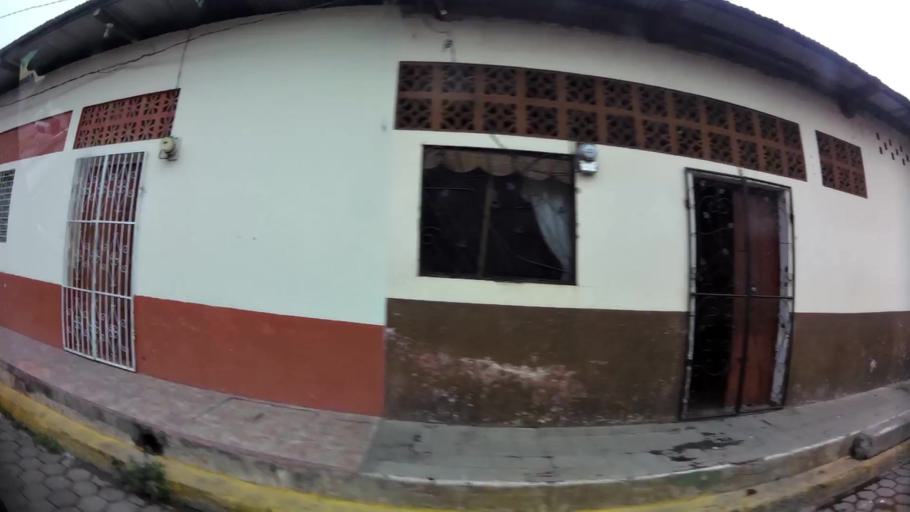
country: NI
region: Leon
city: Leon
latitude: 12.4333
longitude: -86.8757
